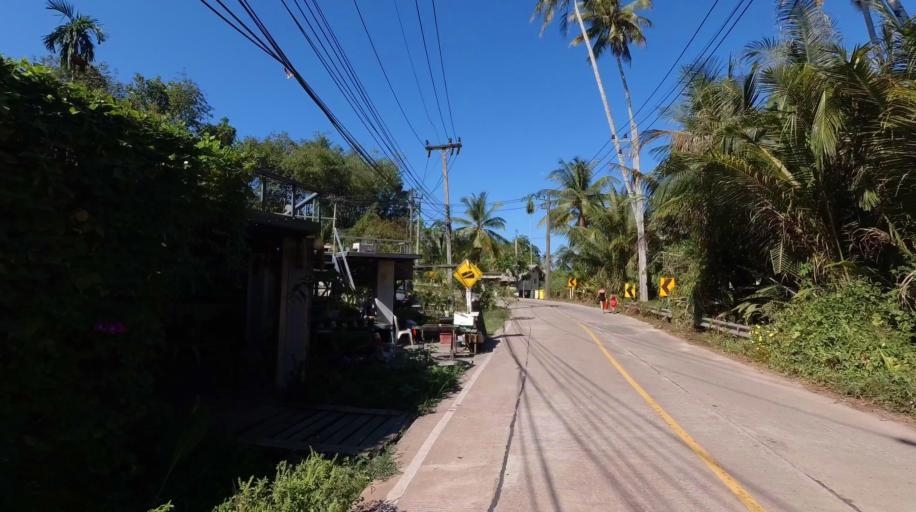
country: TH
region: Trat
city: Ko Kut
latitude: 11.6204
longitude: 102.5455
